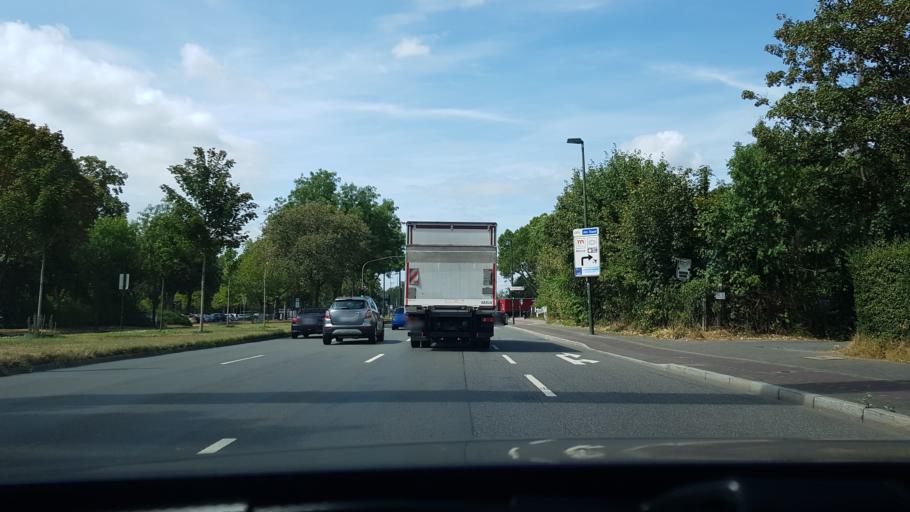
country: DE
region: North Rhine-Westphalia
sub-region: Regierungsbezirk Dusseldorf
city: Dusseldorf
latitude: 51.2010
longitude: 6.7583
